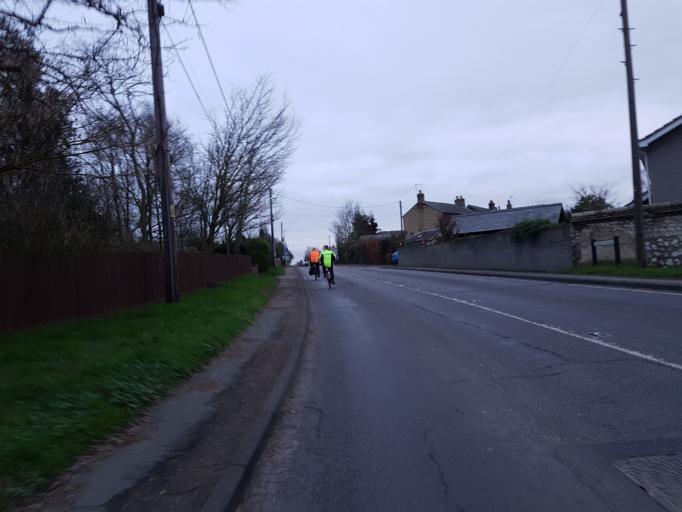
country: GB
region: England
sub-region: Cambridgeshire
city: Fulbourn
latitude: 52.2188
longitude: 0.2189
